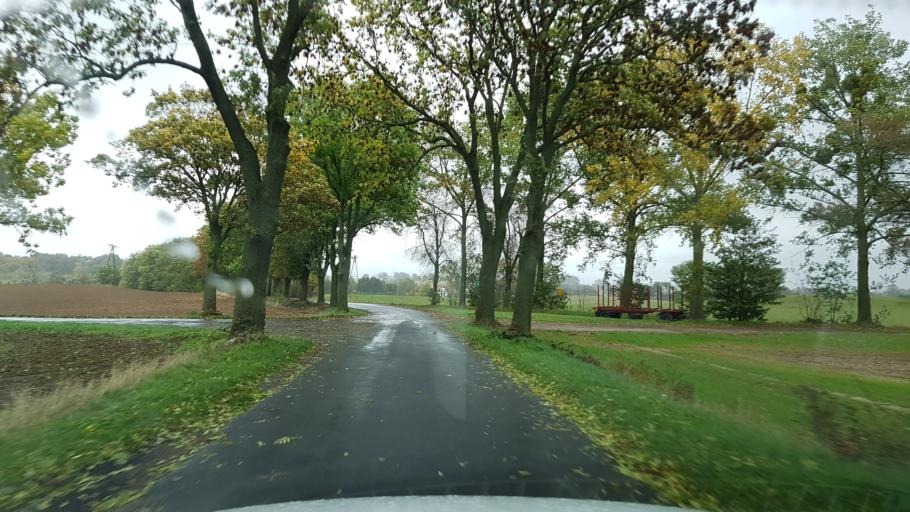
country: PL
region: West Pomeranian Voivodeship
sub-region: Powiat pyrzycki
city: Pyrzyce
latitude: 53.0658
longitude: 14.8933
